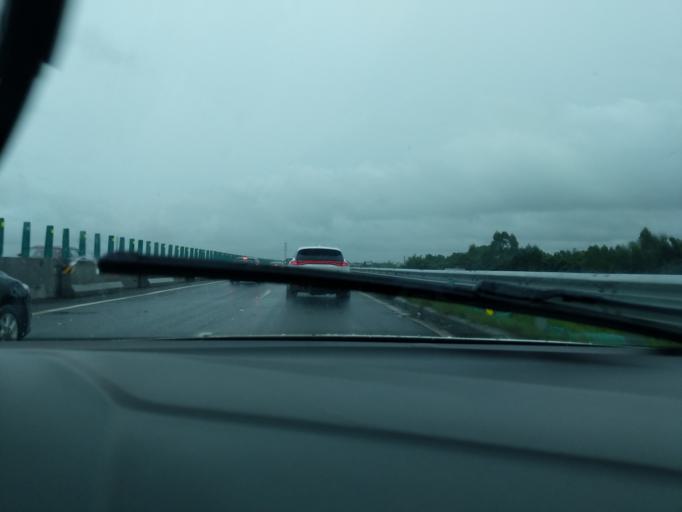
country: CN
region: Guangdong
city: Yueshan
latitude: 22.4618
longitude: 112.6905
